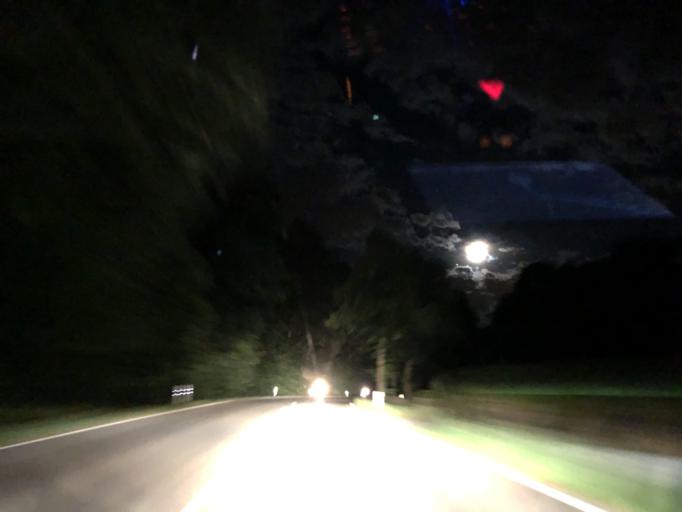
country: DE
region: Bavaria
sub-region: Upper Bavaria
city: Moosinning
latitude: 48.2545
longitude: 11.8501
